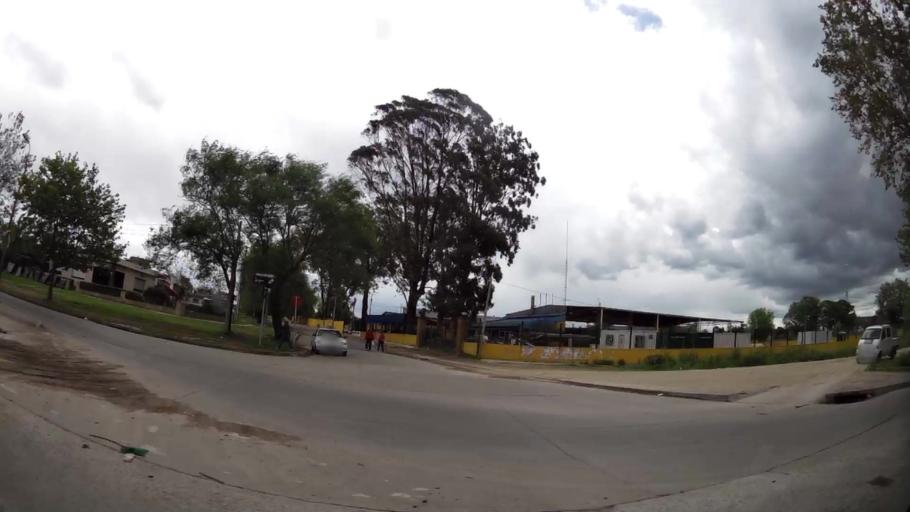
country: UY
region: Canelones
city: Toledo
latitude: -34.8085
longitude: -56.1374
